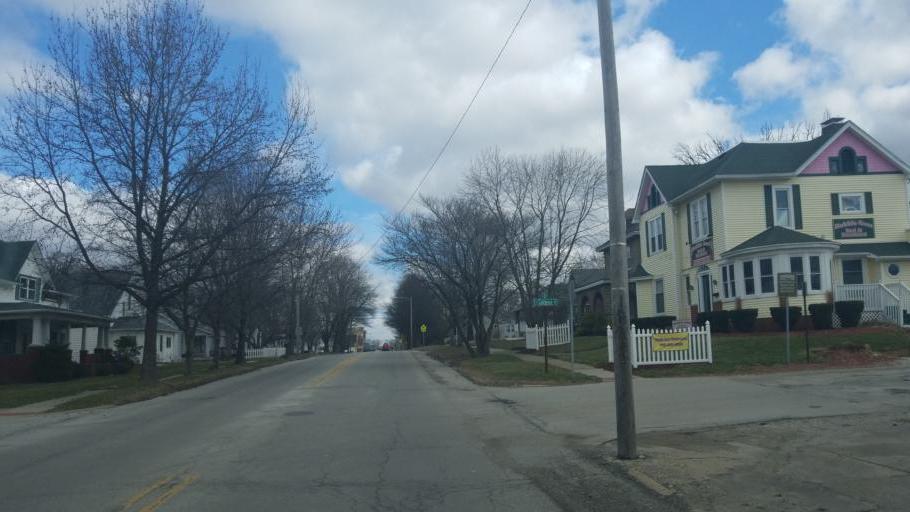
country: US
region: Indiana
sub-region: Parke County
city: Rockville
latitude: 39.7625
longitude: -87.2342
